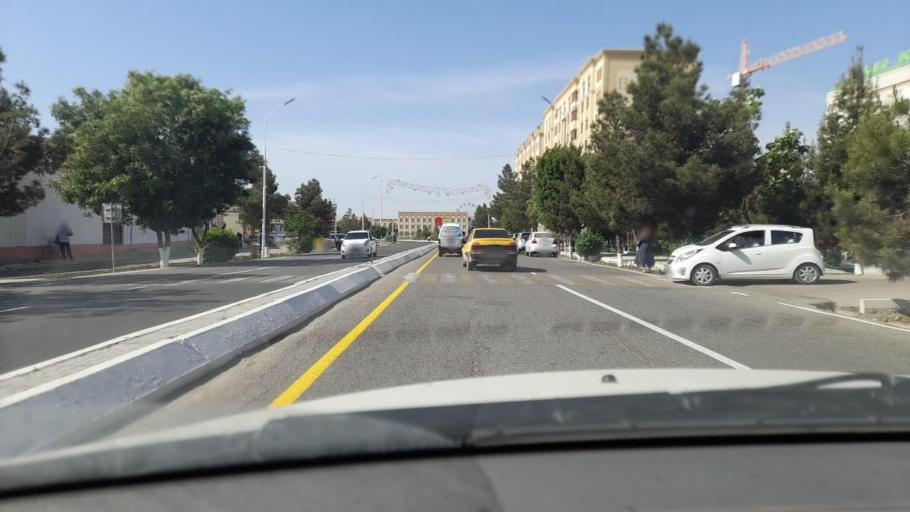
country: UZ
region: Bukhara
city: Bukhara
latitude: 39.7869
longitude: 64.4306
